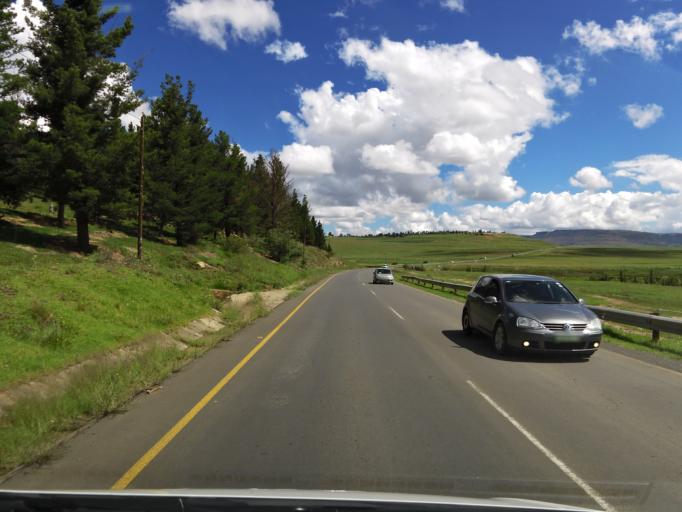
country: LS
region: Maseru
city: Maseru
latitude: -29.5209
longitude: 27.5232
